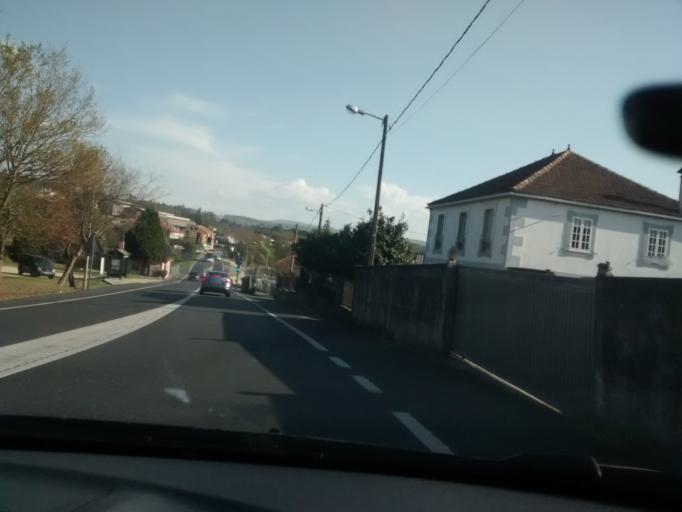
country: ES
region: Galicia
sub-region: Provincia da Coruna
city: Teo
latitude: 42.7667
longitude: -8.5490
